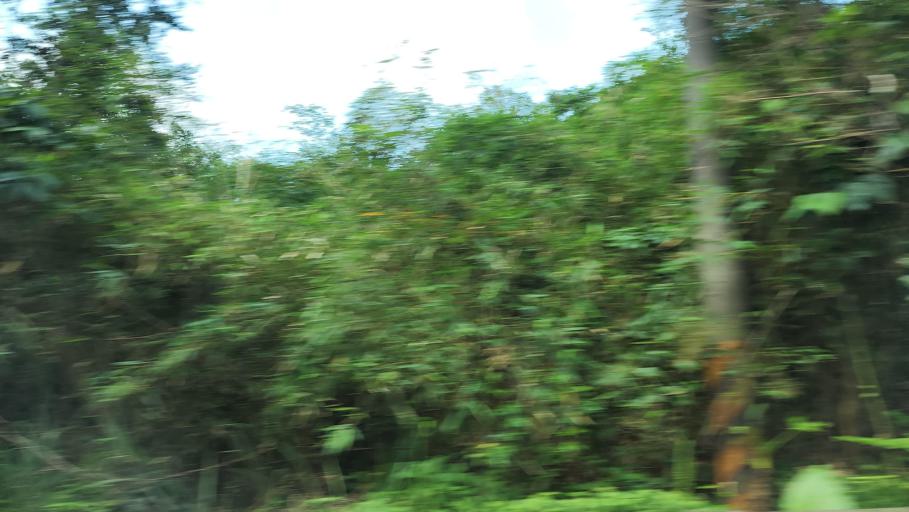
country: TW
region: Taiwan
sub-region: Keelung
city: Keelung
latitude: 25.1850
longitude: 121.6404
